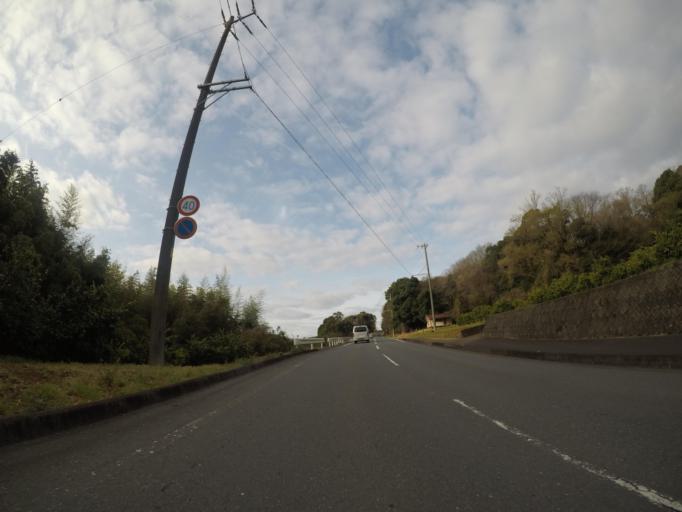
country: JP
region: Shizuoka
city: Hamakita
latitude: 34.8227
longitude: 137.7569
